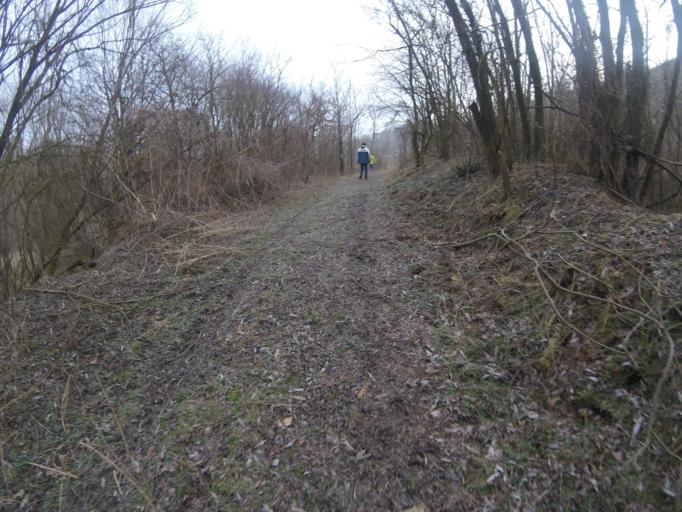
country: HU
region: Baranya
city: Mecseknadasd
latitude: 46.1486
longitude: 18.5152
